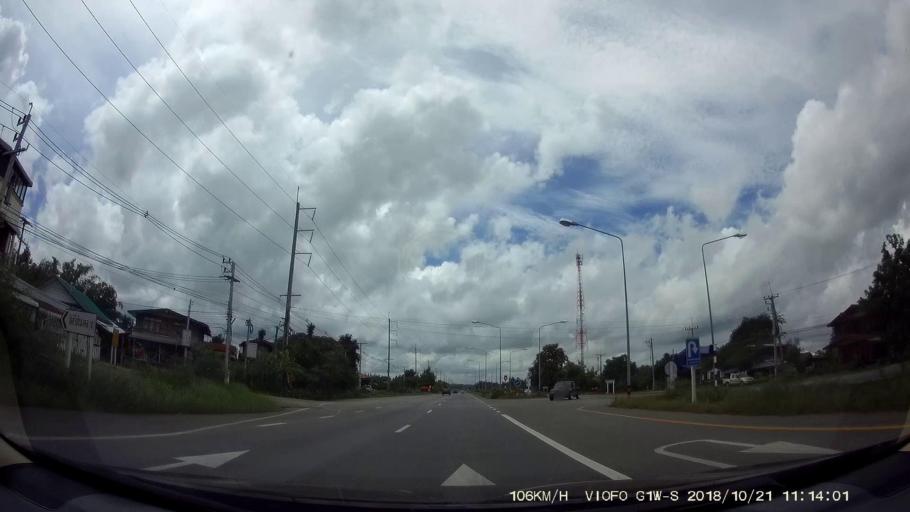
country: TH
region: Chaiyaphum
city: Chaiyaphum
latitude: 15.9093
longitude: 102.1267
